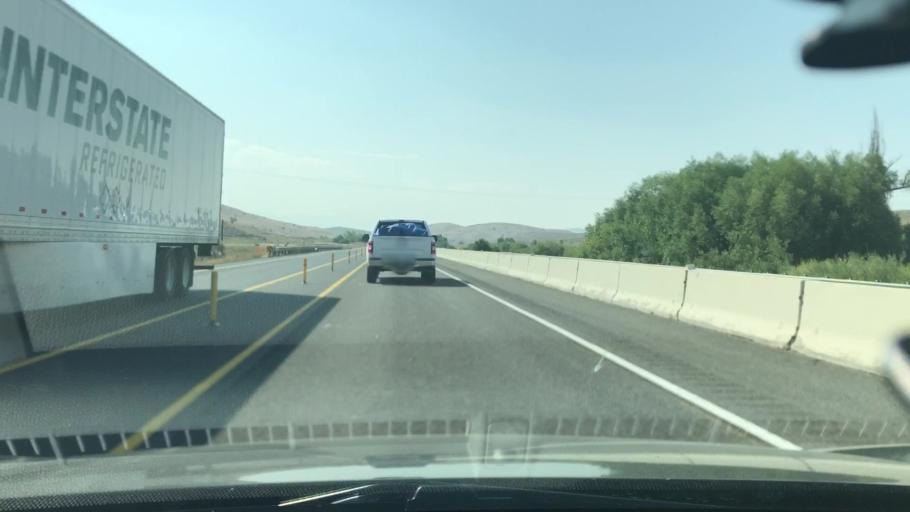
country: US
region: Oregon
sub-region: Baker County
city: Baker City
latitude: 44.6734
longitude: -117.6297
